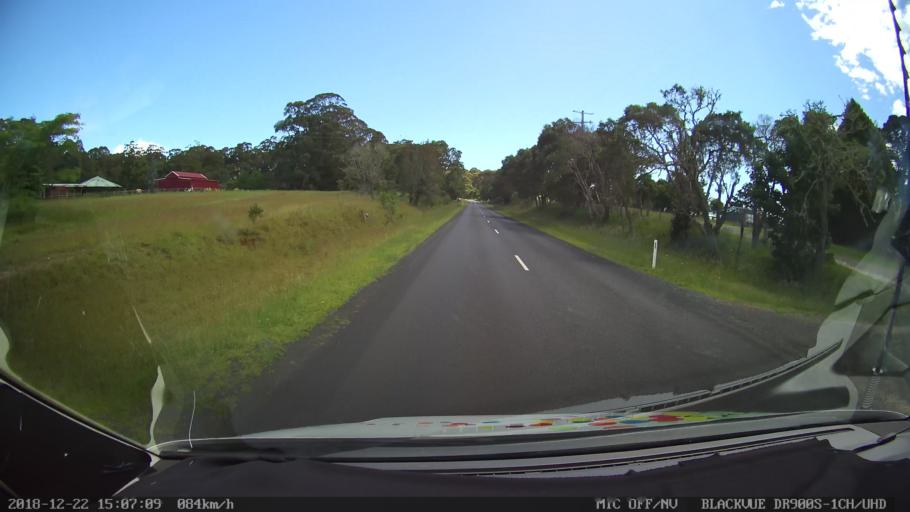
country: AU
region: New South Wales
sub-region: Bellingen
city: Dorrigo
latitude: -30.2981
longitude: 152.4182
